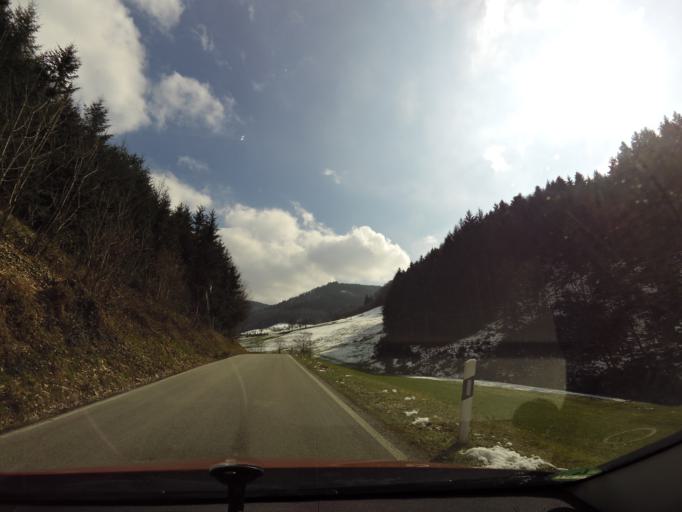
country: DE
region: Baden-Wuerttemberg
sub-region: Freiburg Region
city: Ottenhofen im Schwarzwald
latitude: 48.5518
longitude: 8.1581
